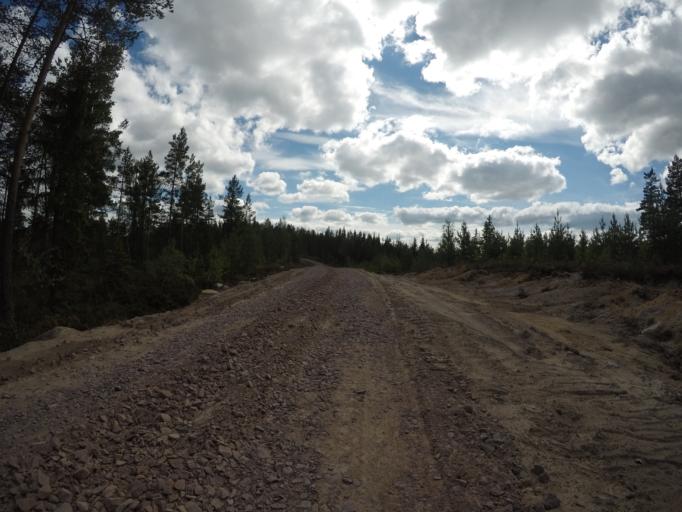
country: SE
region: OErebro
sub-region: Hallefors Kommun
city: Haellefors
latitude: 60.0723
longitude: 14.4751
